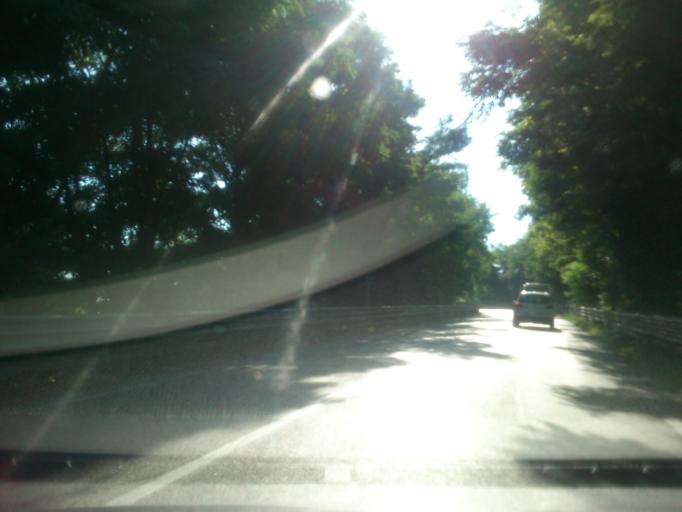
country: IT
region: The Marches
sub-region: Provincia di Pesaro e Urbino
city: Pesaro
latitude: 43.9101
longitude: 12.8735
